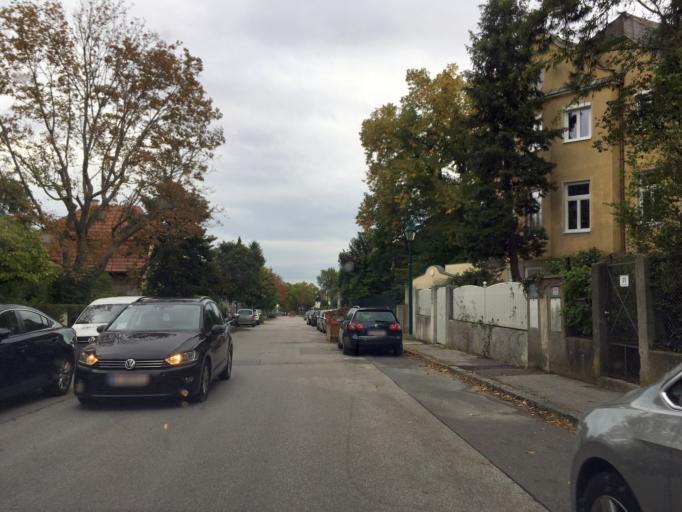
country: AT
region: Lower Austria
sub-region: Politischer Bezirk Modling
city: Maria Enzersdorf
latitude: 48.0957
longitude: 16.2777
